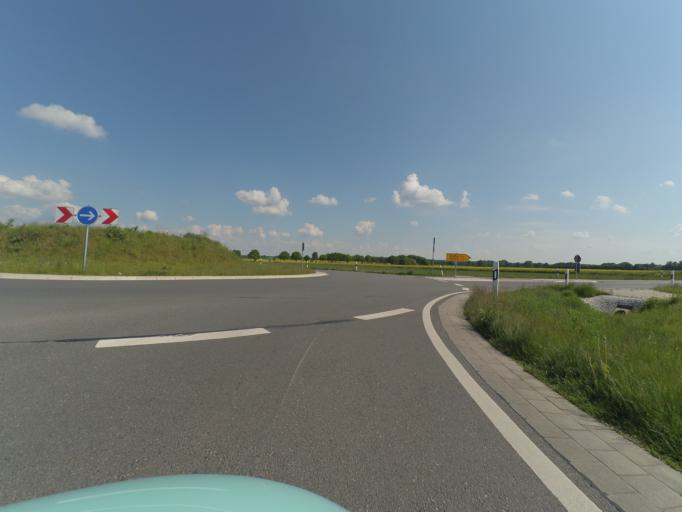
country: DE
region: Lower Saxony
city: Isernhagen Farster Bauerschaft
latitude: 52.4797
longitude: 9.8977
